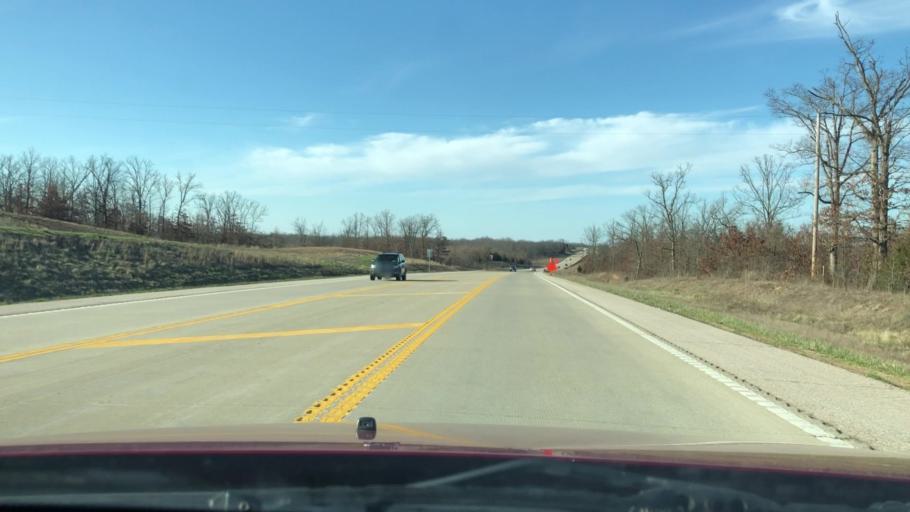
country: US
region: Missouri
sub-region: Camden County
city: Camdenton
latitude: 37.9374
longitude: -92.7153
